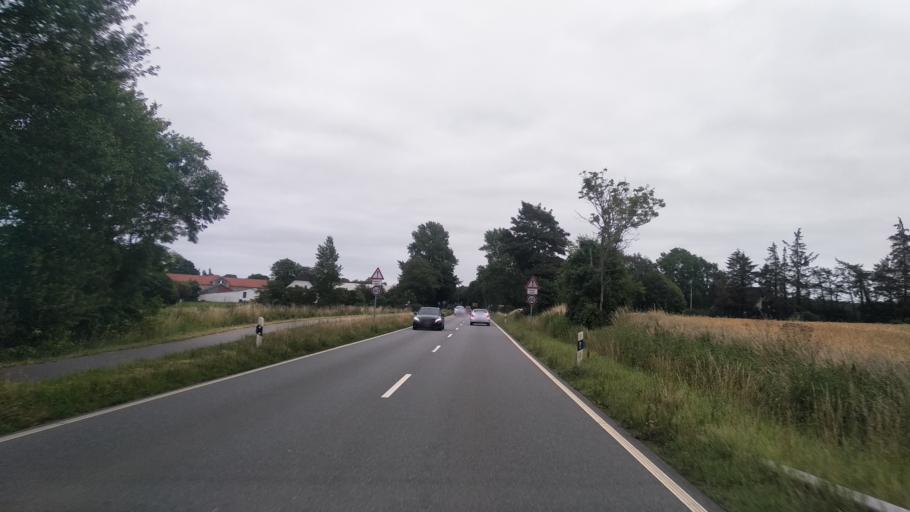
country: DE
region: Schleswig-Holstein
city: Langballig
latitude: 54.7986
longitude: 9.6272
